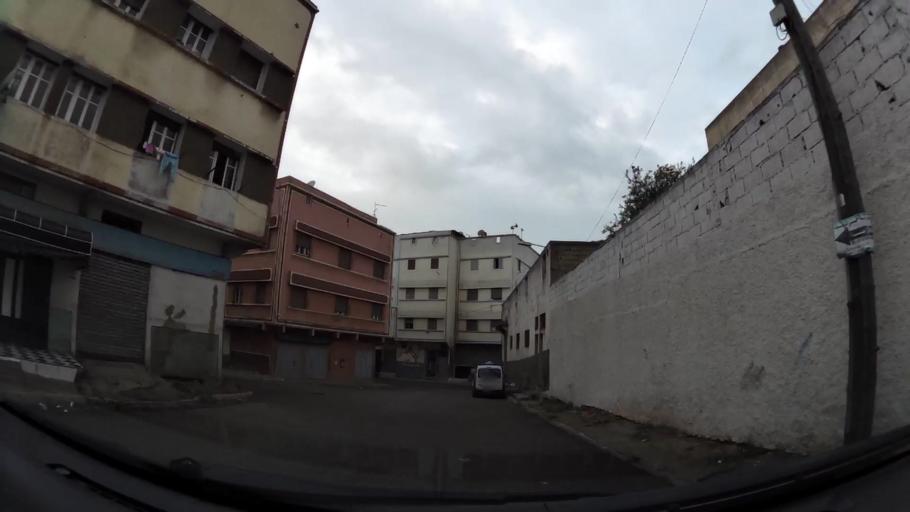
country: MA
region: Grand Casablanca
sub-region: Casablanca
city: Casablanca
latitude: 33.5580
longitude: -7.5969
